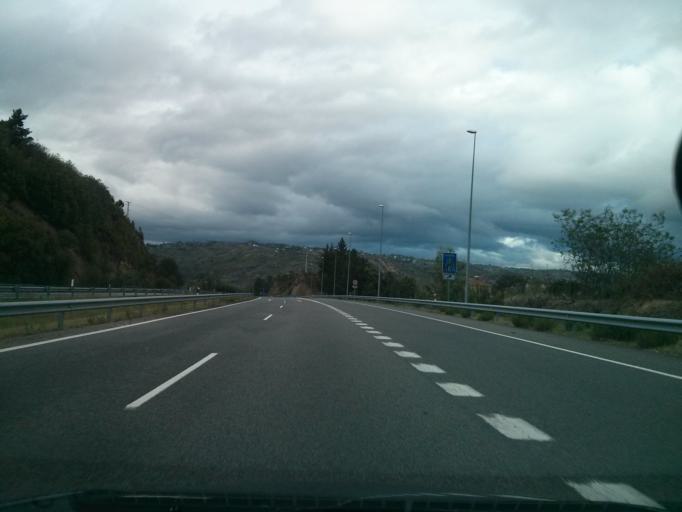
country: ES
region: Galicia
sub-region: Provincia de Ourense
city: Ourense
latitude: 42.3394
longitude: -7.8848
